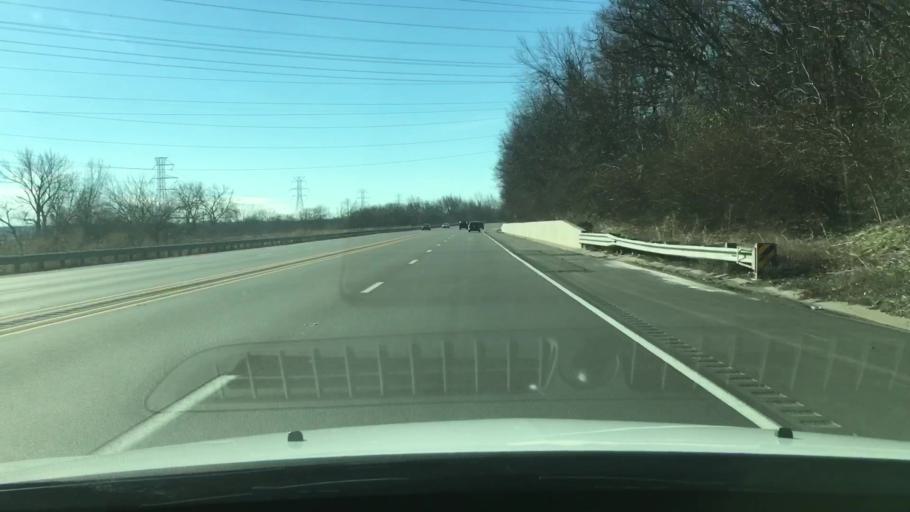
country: US
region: Illinois
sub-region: Tazewell County
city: Pekin
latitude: 40.5963
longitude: -89.6715
